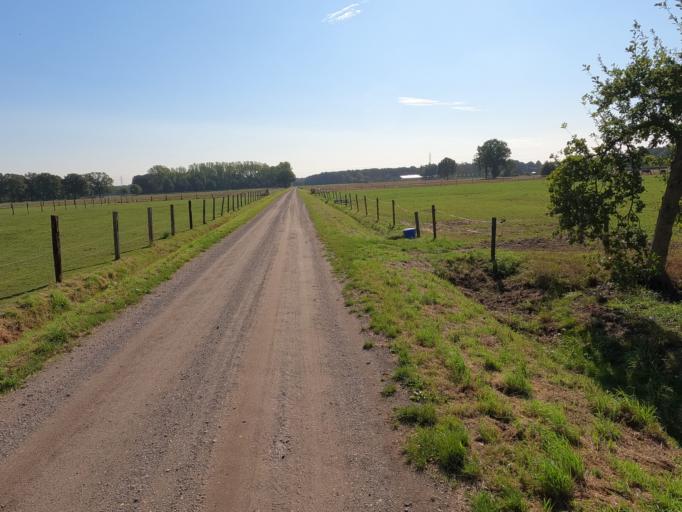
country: BE
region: Flanders
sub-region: Provincie Antwerpen
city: Zoersel
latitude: 51.2356
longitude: 4.7098
